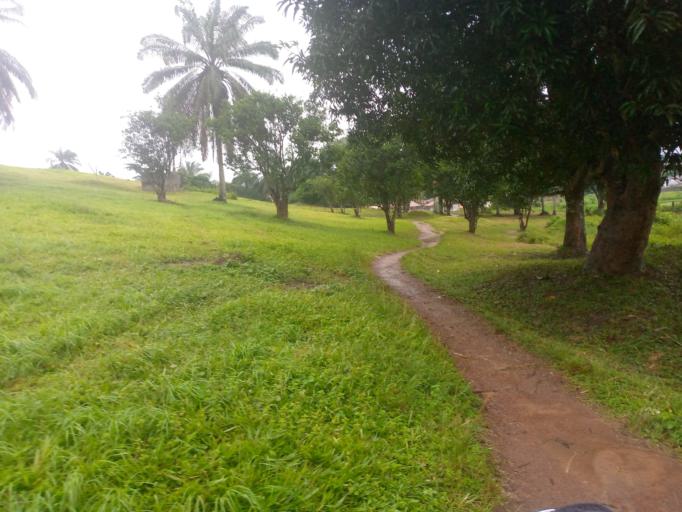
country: SL
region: Eastern Province
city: Kenema
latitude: 7.8783
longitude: -11.1760
